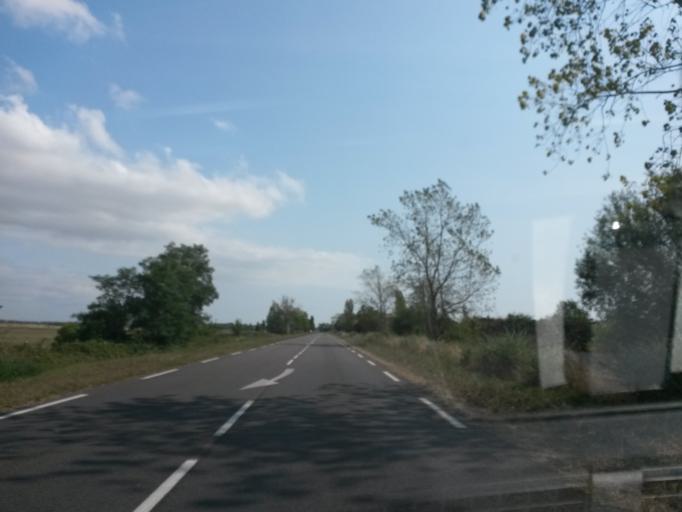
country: FR
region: Pays de la Loire
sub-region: Departement de la Vendee
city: La Tranche-sur-Mer
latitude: 46.3602
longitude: -1.4485
